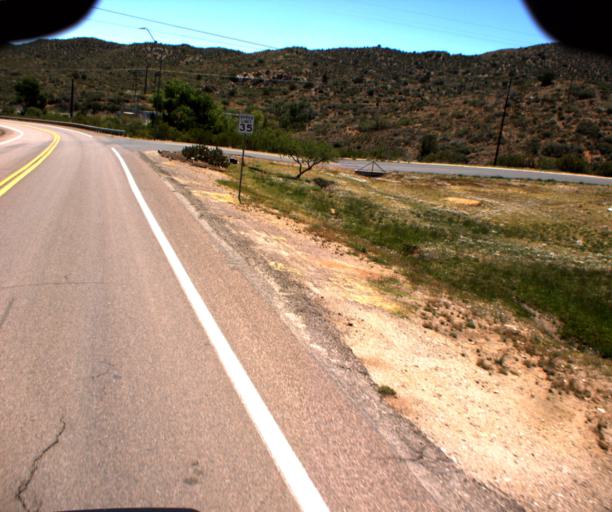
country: US
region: Arizona
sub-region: Yavapai County
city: Bagdad
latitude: 34.5680
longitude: -113.1755
